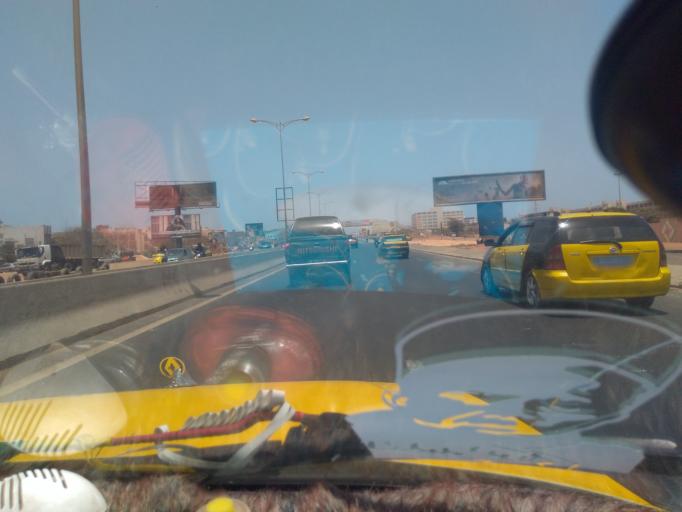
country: SN
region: Dakar
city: Grand Dakar
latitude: 14.7447
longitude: -17.4526
